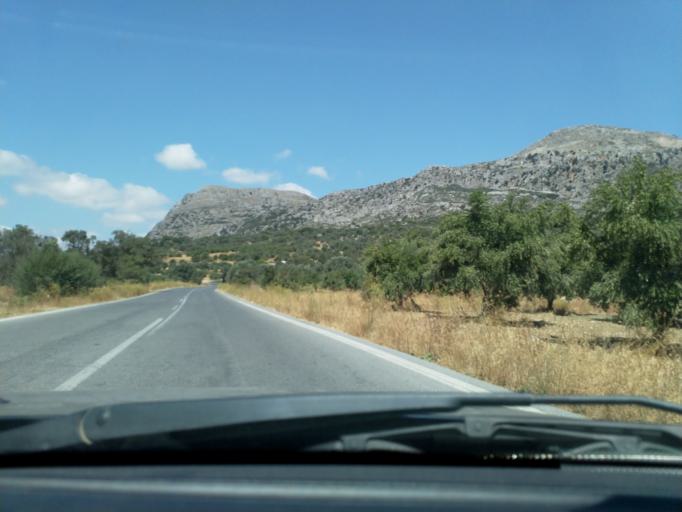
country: GR
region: Crete
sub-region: Nomos Rethymnis
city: Agia Foteini
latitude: 35.1918
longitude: 24.5521
